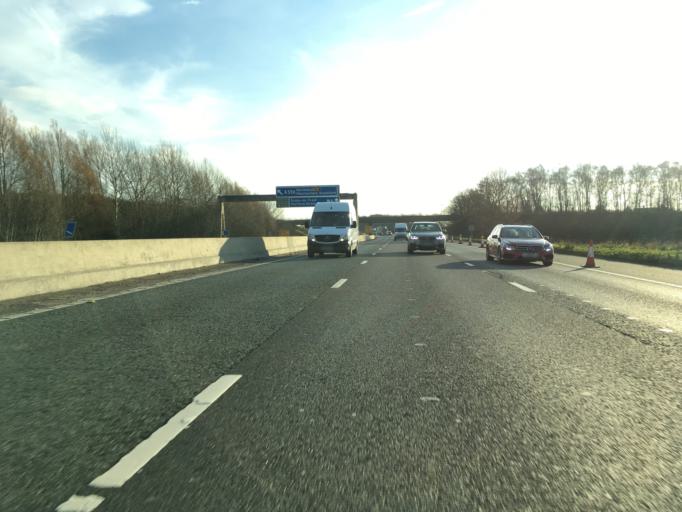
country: GB
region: England
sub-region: Cheshire East
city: Mere
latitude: 53.3151
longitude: -2.4264
